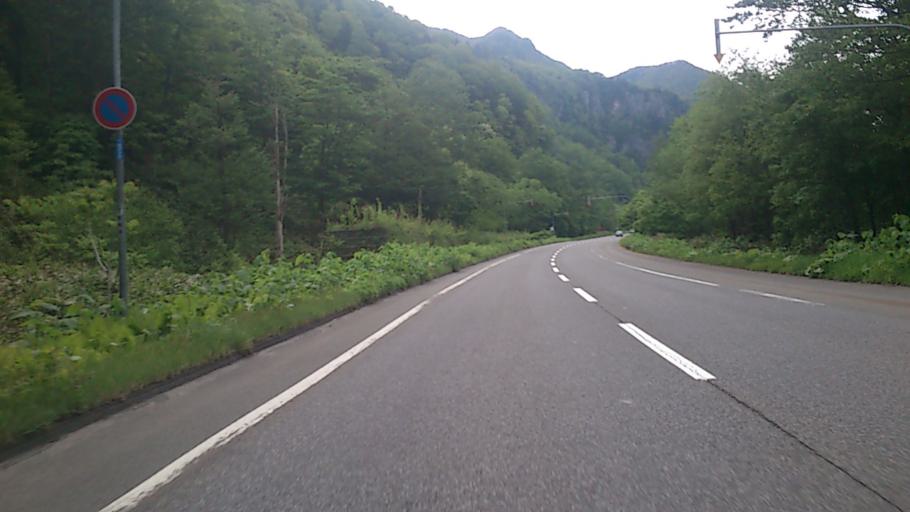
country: JP
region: Hokkaido
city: Kamikawa
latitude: 43.7569
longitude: 142.9247
